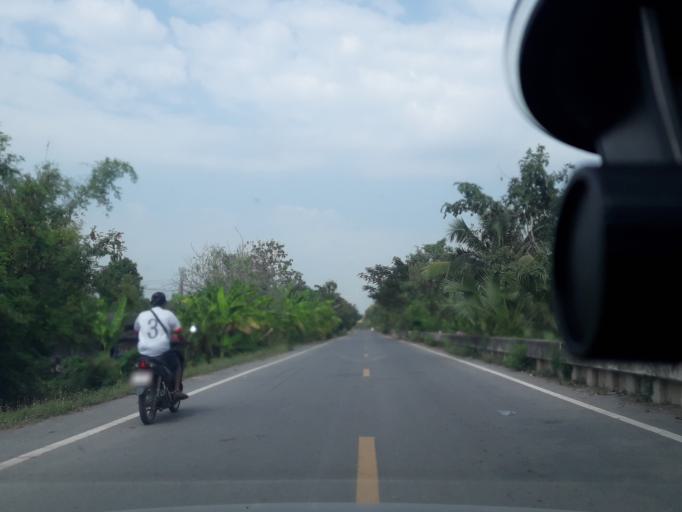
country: TH
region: Sara Buri
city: Nong Khae
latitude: 14.2398
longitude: 100.8914
